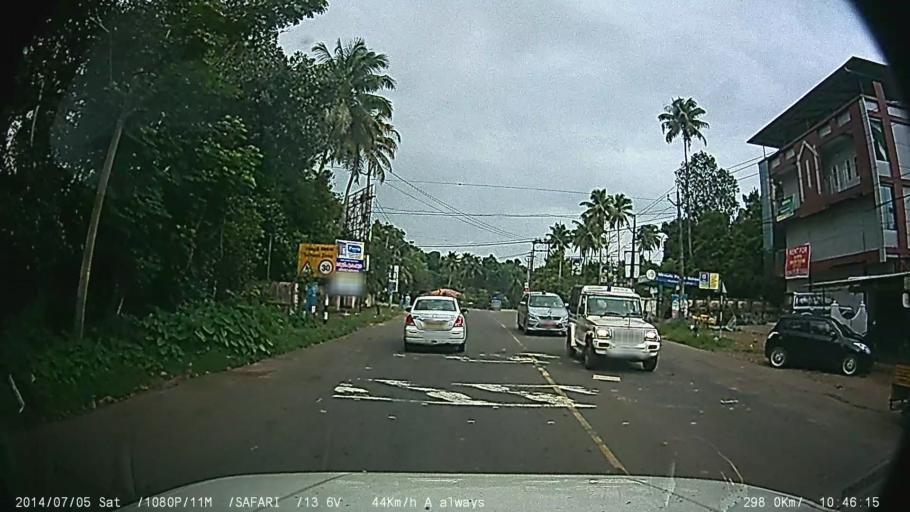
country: IN
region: Kerala
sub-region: Ernakulam
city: Muvattupula
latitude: 9.9744
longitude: 76.5962
